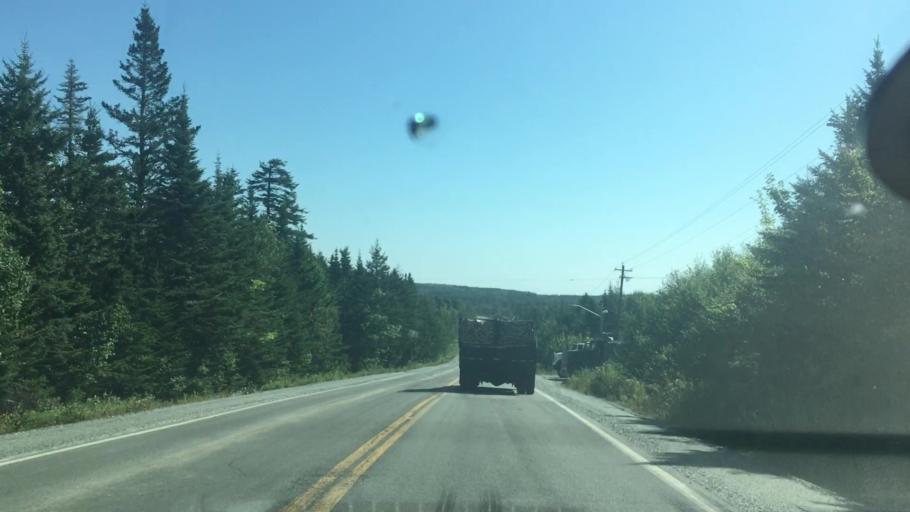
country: CA
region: Nova Scotia
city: New Glasgow
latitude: 44.9045
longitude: -62.4671
